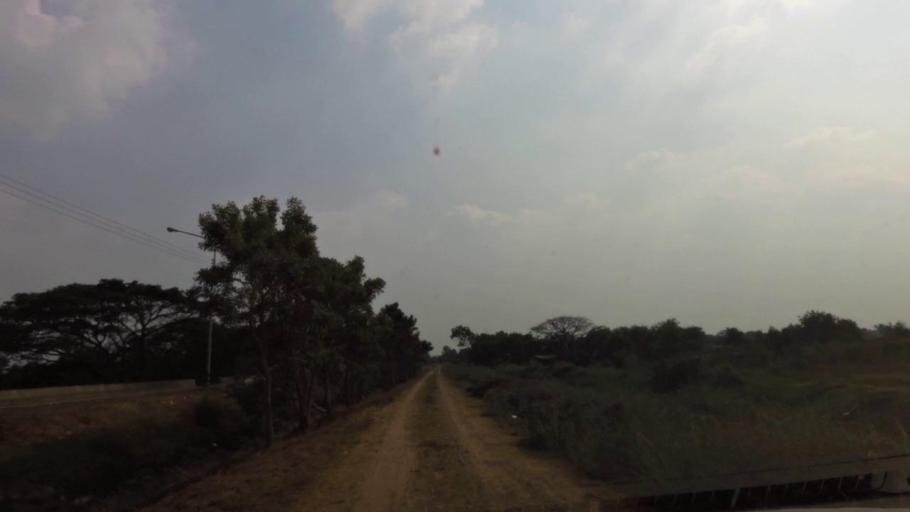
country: TH
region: Phra Nakhon Si Ayutthaya
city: Phra Nakhon Si Ayutthaya
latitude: 14.3156
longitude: 100.5614
